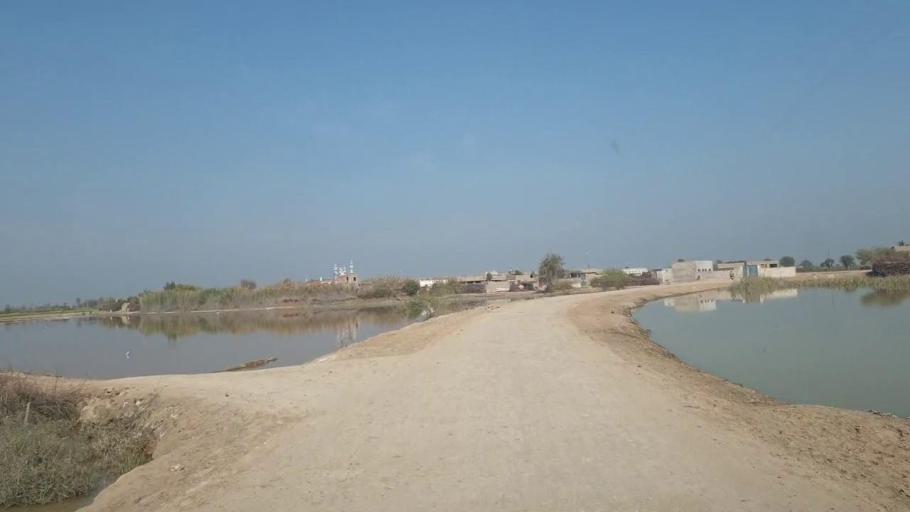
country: PK
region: Sindh
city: Sakrand
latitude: 26.0695
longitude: 68.4143
